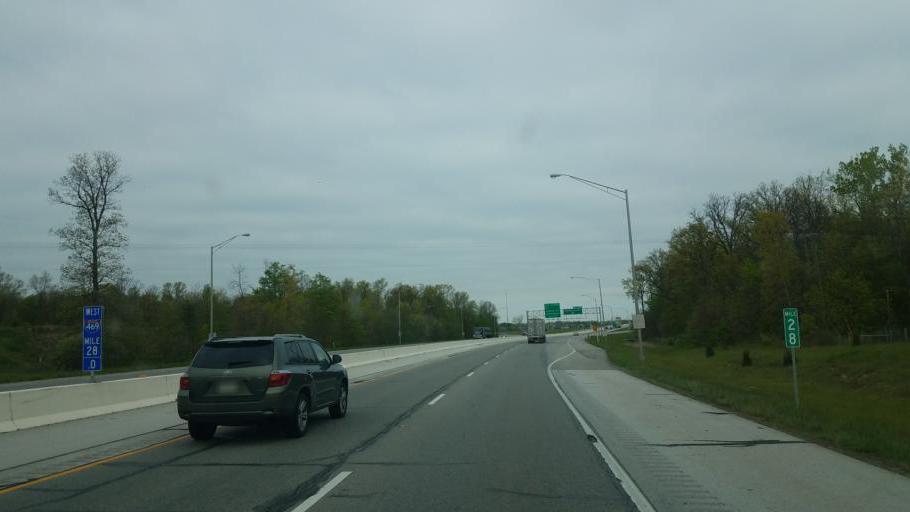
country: US
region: Indiana
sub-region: Allen County
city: Leo-Cedarville
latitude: 41.1572
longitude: -85.0530
